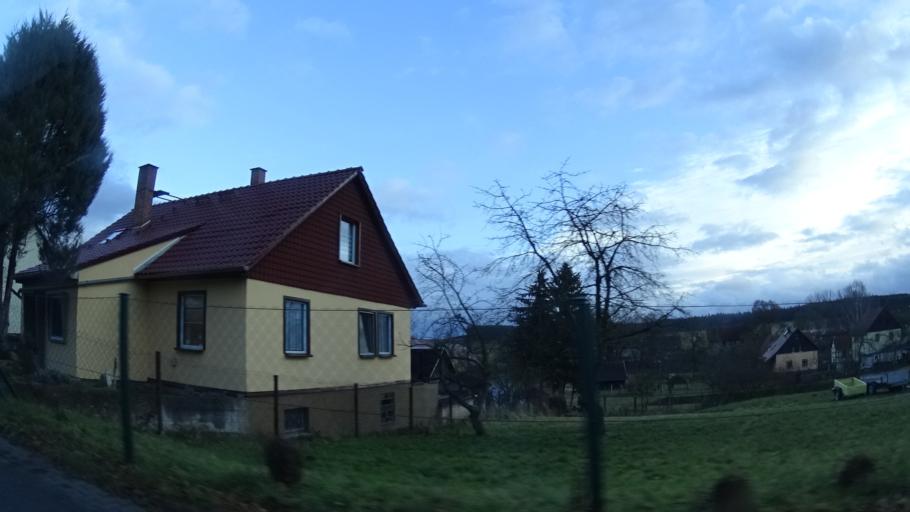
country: DE
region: Thuringia
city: Stadtilm
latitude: 50.7269
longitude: 11.0592
